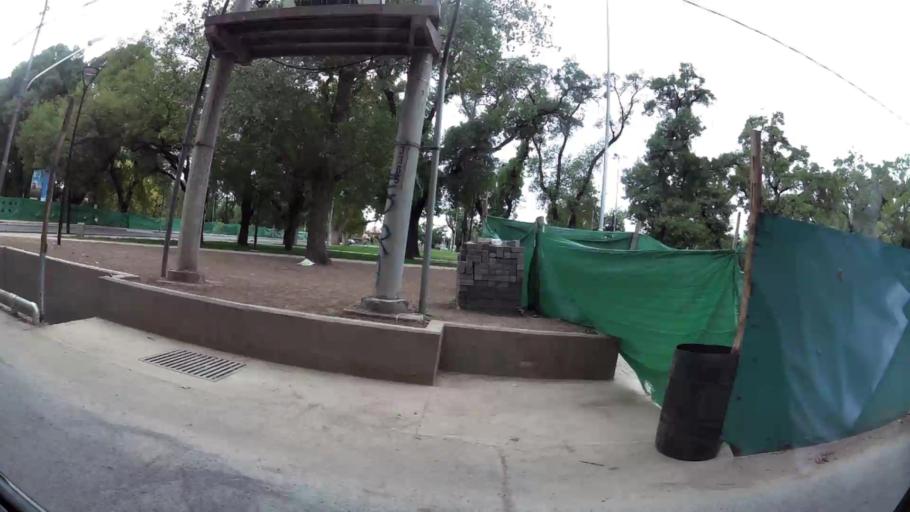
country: AR
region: Mendoza
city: Mendoza
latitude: -32.8854
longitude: -68.8298
